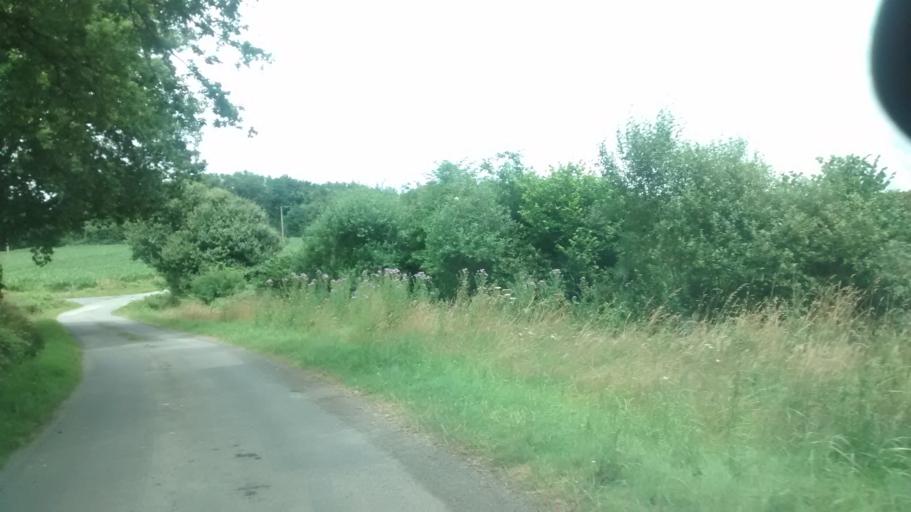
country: FR
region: Brittany
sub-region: Departement d'Ille-et-Vilaine
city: La Dominelais
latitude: 47.7807
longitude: -1.7271
